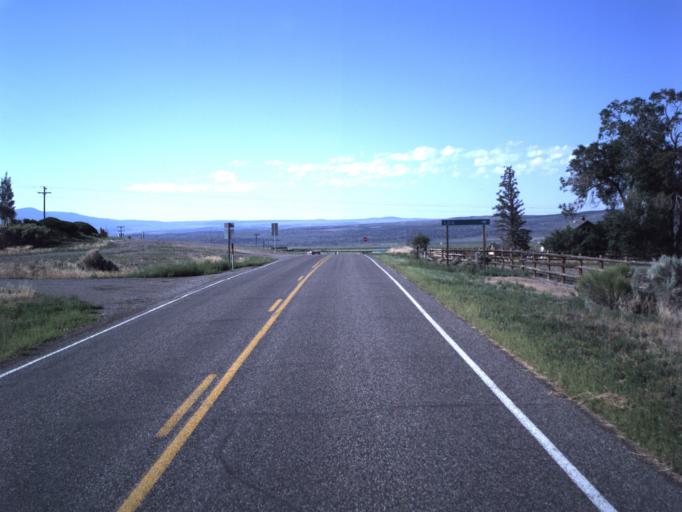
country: US
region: Utah
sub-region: Wayne County
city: Loa
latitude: 38.4131
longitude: -111.6204
